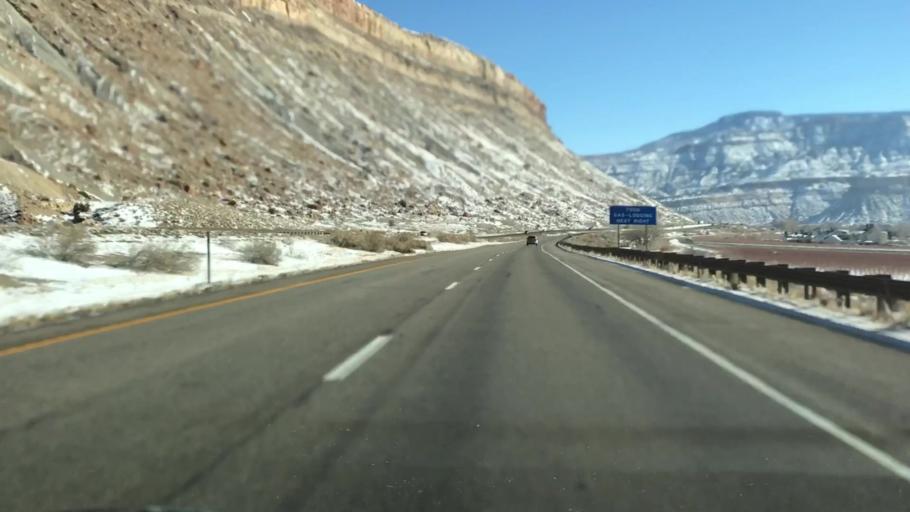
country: US
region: Colorado
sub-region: Mesa County
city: Palisade
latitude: 39.1203
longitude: -108.3724
